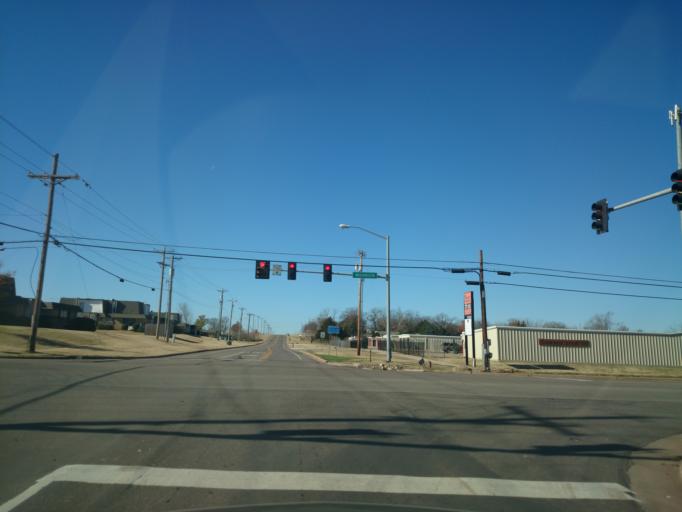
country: US
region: Oklahoma
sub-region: Payne County
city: Stillwater
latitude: 36.1595
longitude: -97.0695
